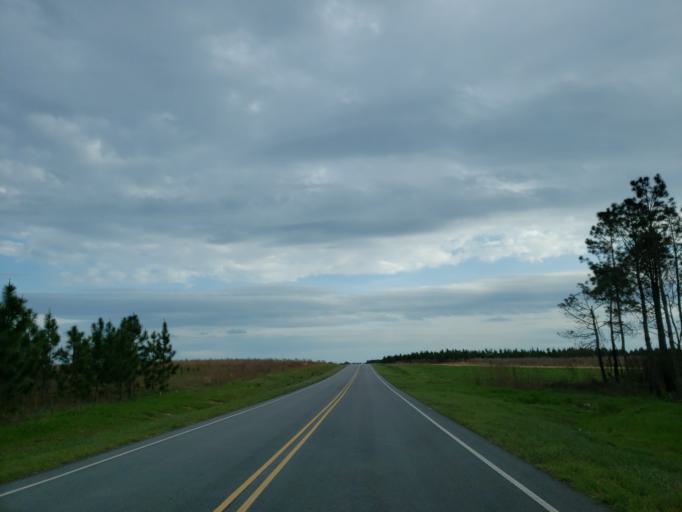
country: US
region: Georgia
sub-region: Dooly County
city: Vienna
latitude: 32.1188
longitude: -83.7562
